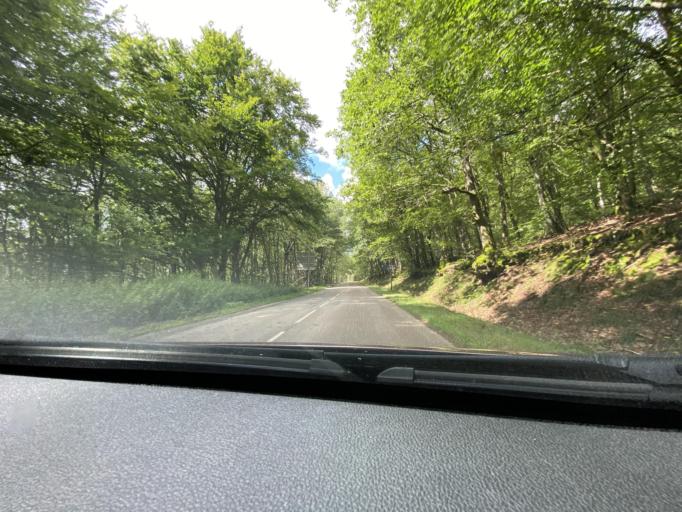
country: FR
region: Bourgogne
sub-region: Departement de la Cote-d'Or
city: Saulieu
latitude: 47.2526
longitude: 4.0715
